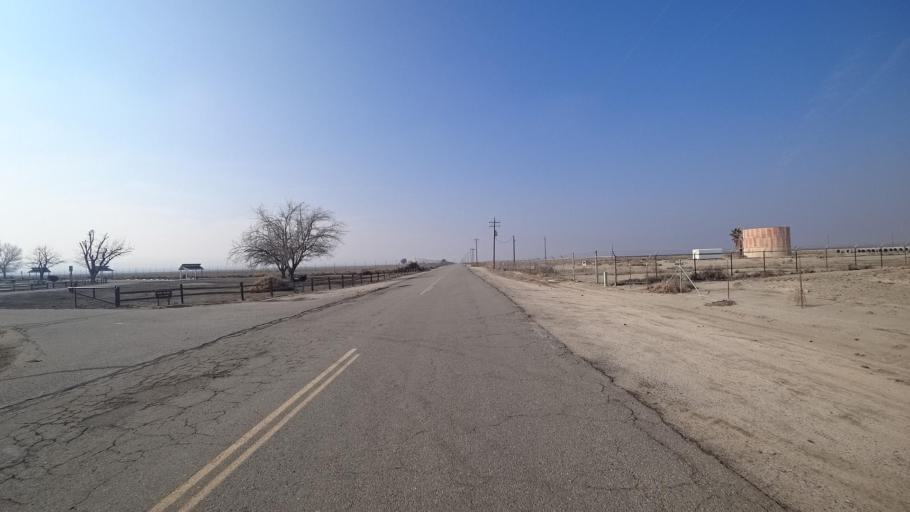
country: US
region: California
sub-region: Kern County
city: Buttonwillow
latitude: 35.3331
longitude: -119.3632
